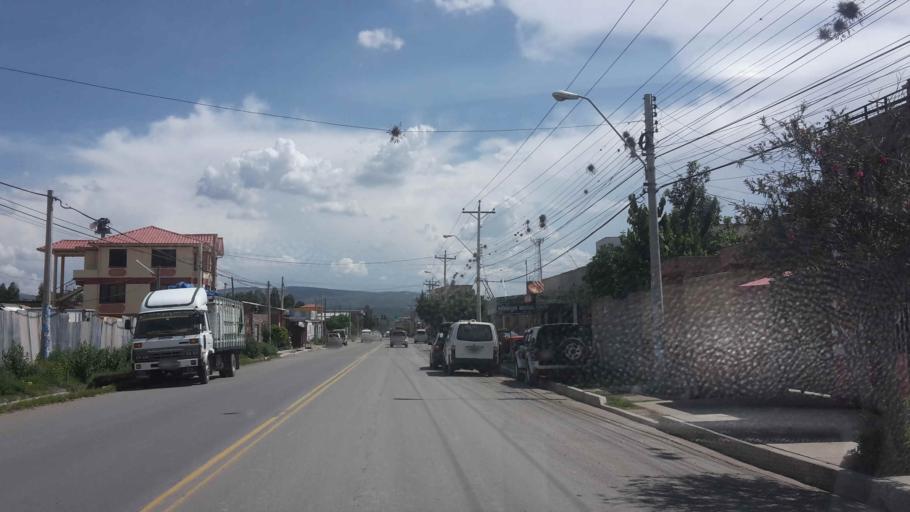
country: BO
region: Cochabamba
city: Cochabamba
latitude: -17.3823
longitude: -66.2360
